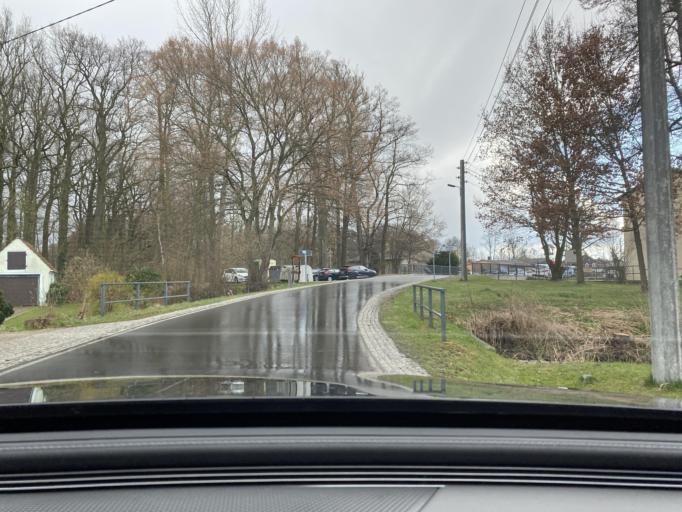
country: DE
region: Saxony
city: Grossdubrau
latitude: 51.3034
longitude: 14.4569
